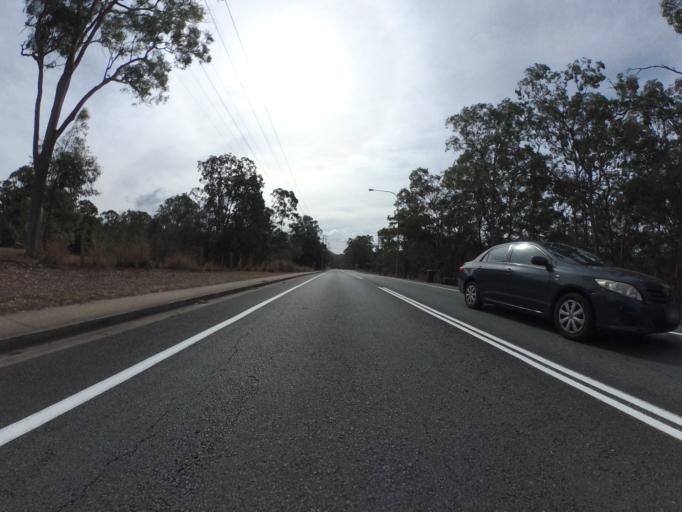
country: AU
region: Queensland
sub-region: Brisbane
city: Riverhills
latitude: -27.5569
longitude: 152.8879
